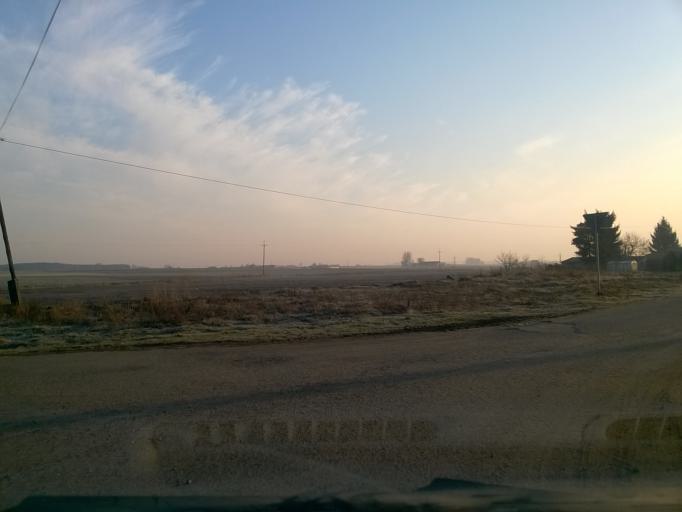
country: PL
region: Kujawsko-Pomorskie
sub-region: Powiat sepolenski
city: Sosno
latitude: 53.4484
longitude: 17.6951
